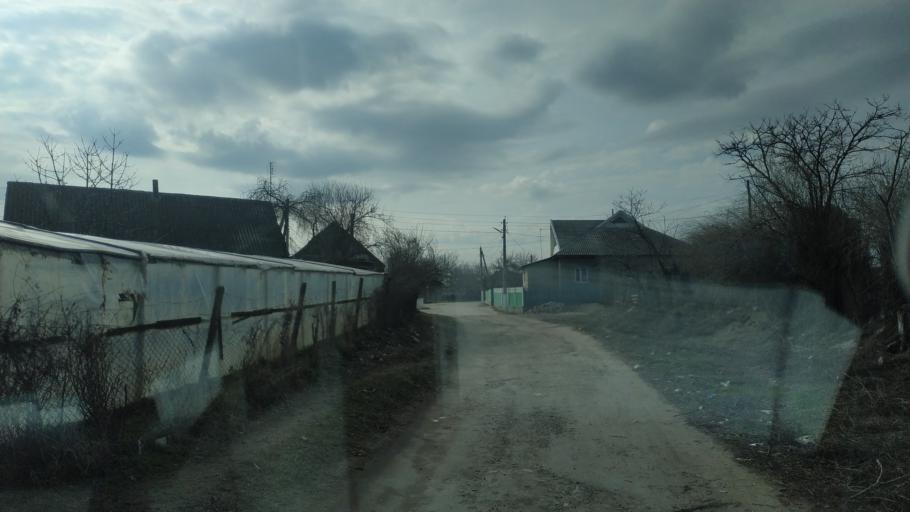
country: MD
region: Anenii Noi
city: Anenii Noi
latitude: 46.9066
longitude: 29.1439
